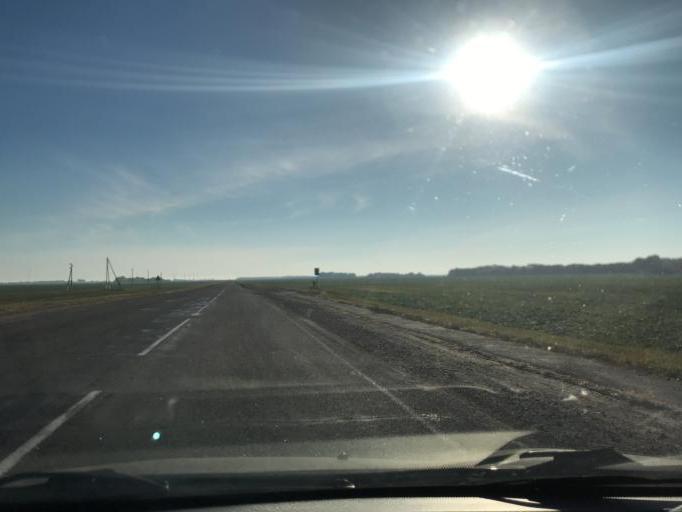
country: BY
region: Gomel
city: Brahin
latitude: 51.7969
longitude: 30.1457
